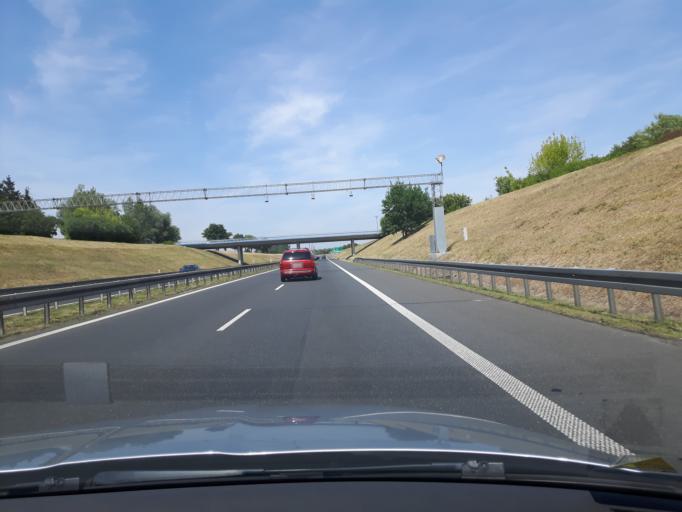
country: PL
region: Masovian Voivodeship
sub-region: Powiat nowodworski
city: Zakroczym
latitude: 52.4330
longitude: 20.6511
